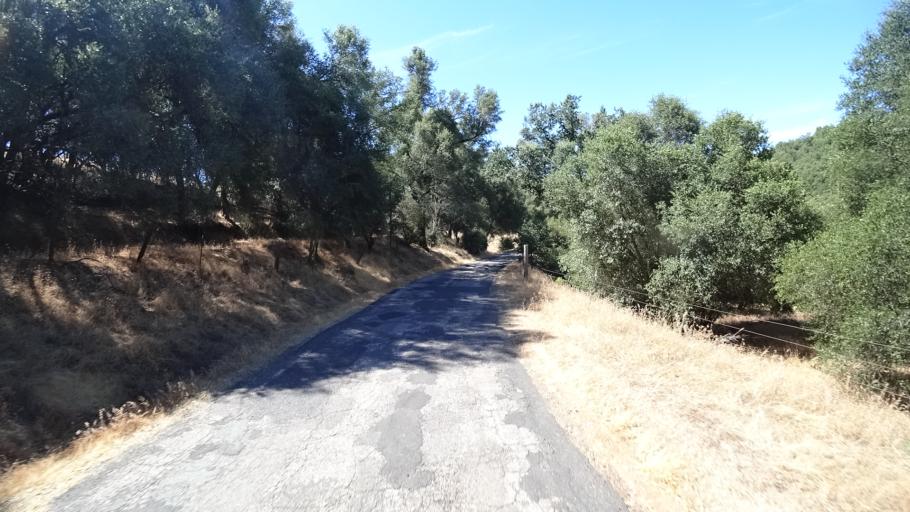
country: US
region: California
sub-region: Calaveras County
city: Angels Camp
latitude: 38.1297
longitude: -120.5686
